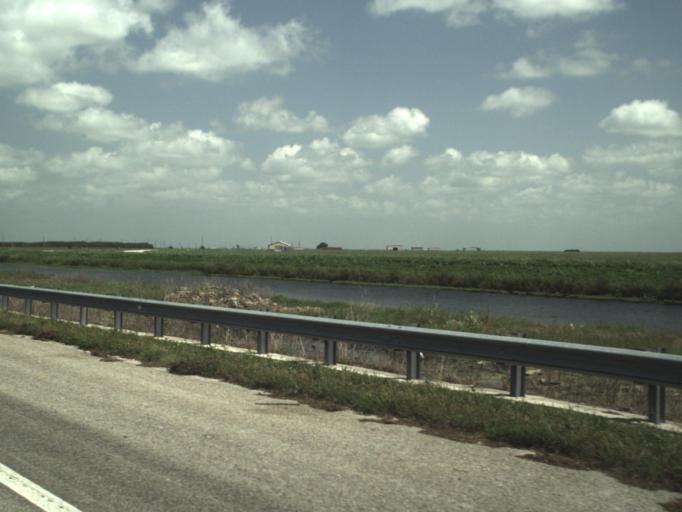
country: US
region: Florida
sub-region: Palm Beach County
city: Belle Glade Camp
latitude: 26.5549
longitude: -80.7086
